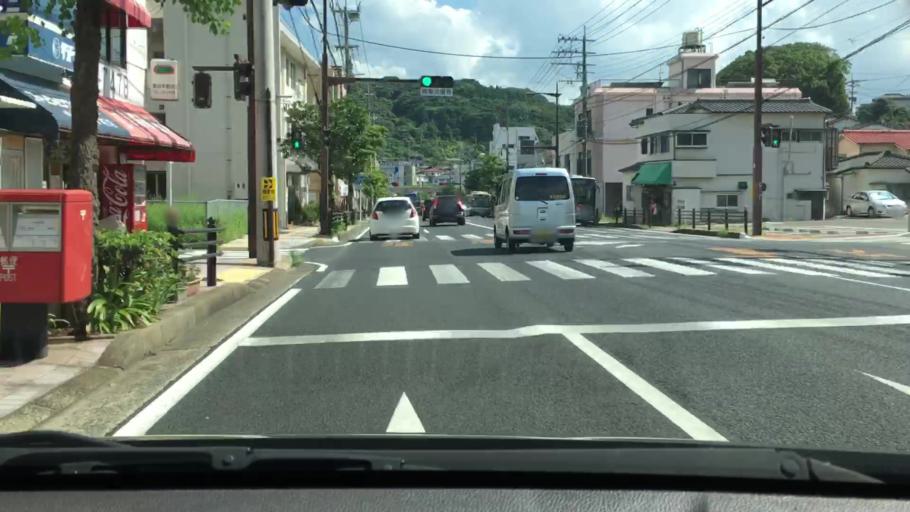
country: JP
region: Nagasaki
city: Sasebo
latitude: 33.1999
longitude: 129.7217
